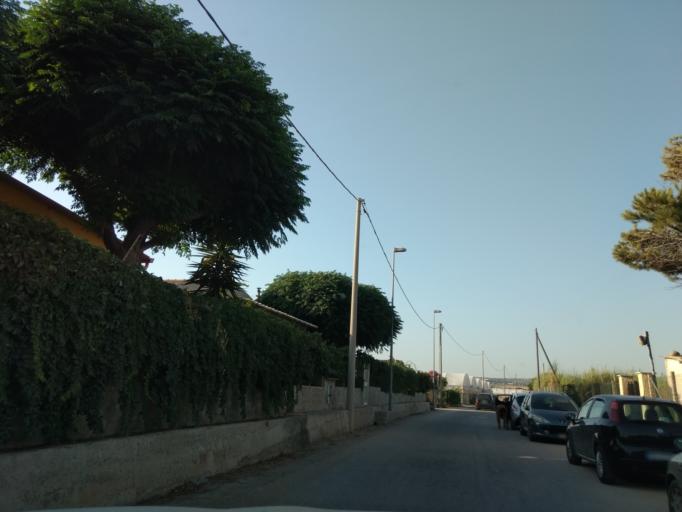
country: IT
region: Sicily
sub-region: Ragusa
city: Donnalucata
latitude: 36.7481
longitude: 14.6632
